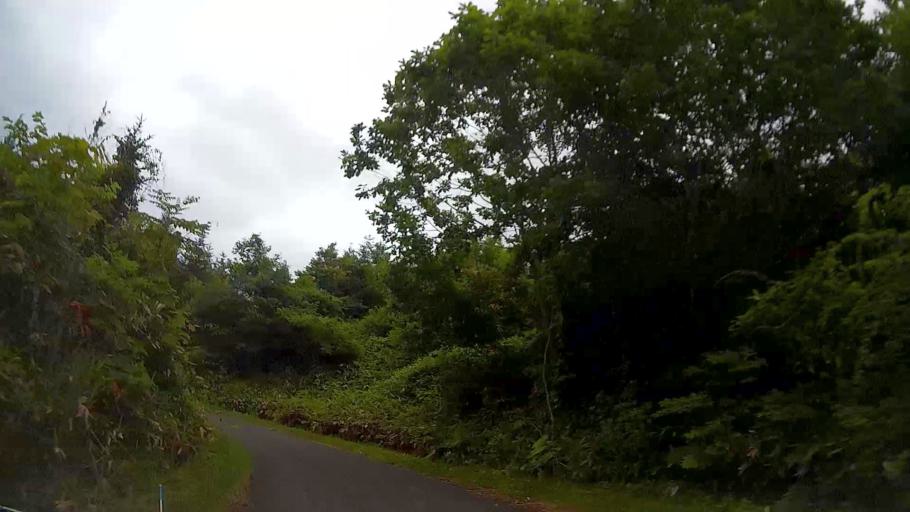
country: JP
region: Hokkaido
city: Nanae
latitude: 42.1262
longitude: 140.4293
